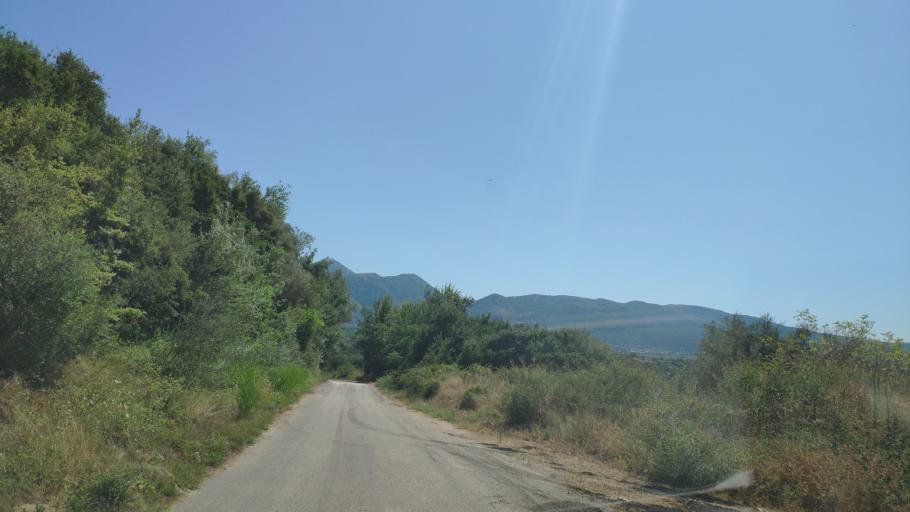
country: GR
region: Epirus
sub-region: Nomos Prevezis
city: Kanalaki
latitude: 39.2716
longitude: 20.6001
